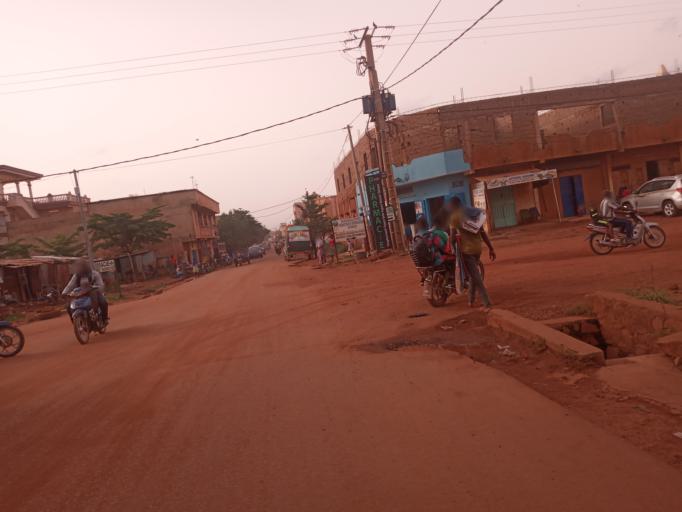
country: ML
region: Bamako
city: Bamako
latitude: 12.5581
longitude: -7.9902
